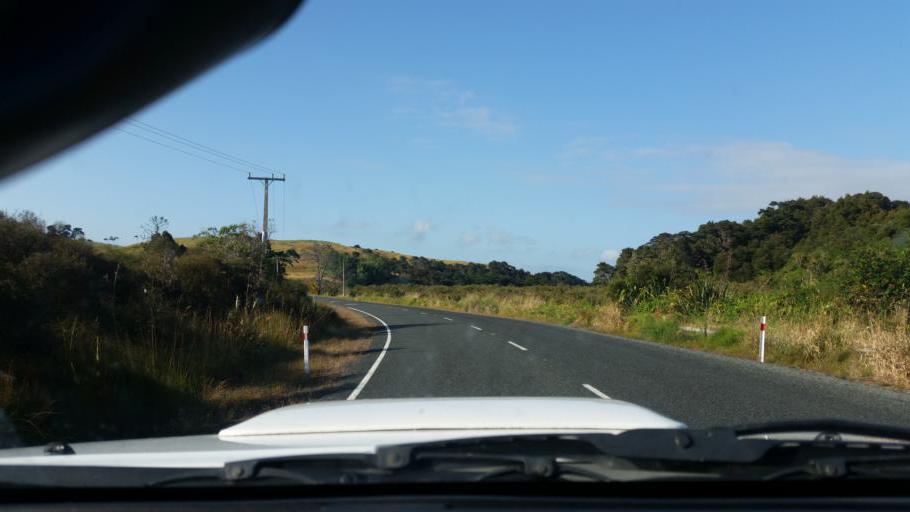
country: NZ
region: Northland
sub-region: Whangarei
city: Ruakaka
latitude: -36.1129
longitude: 174.2295
